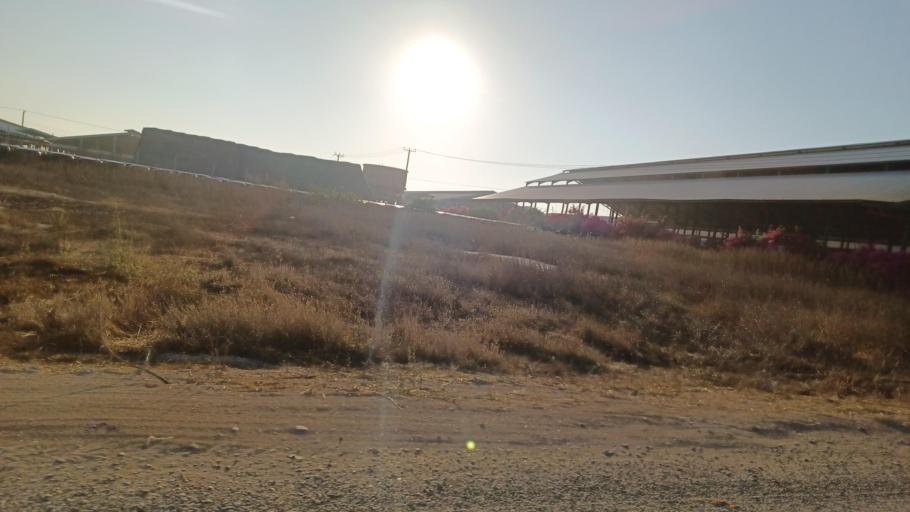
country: CY
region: Ammochostos
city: Achna
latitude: 35.0179
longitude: 33.7996
